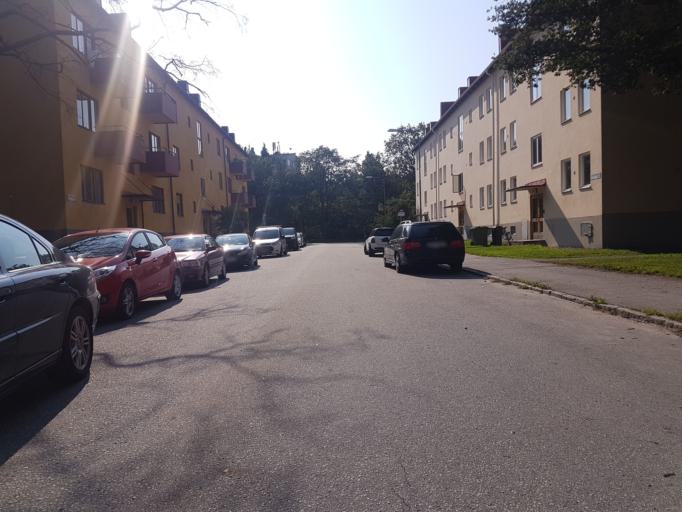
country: SE
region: Stockholm
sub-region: Stockholms Kommun
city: OEstermalm
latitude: 59.2984
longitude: 18.0941
